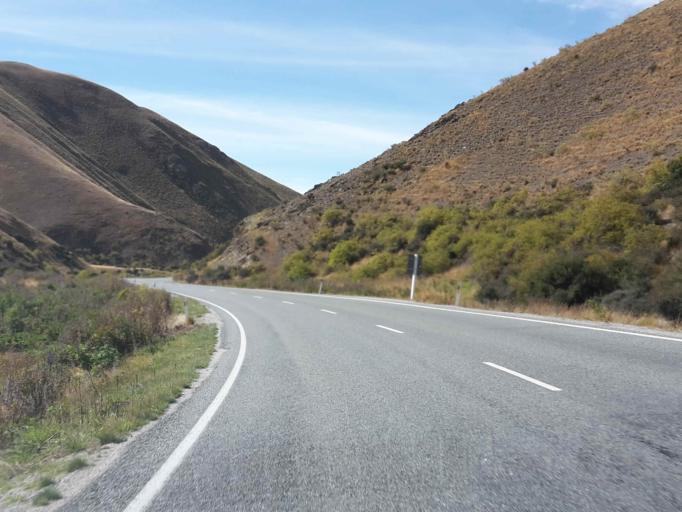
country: NZ
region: Otago
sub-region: Queenstown-Lakes District
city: Wanaka
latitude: -44.5637
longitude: 169.6660
